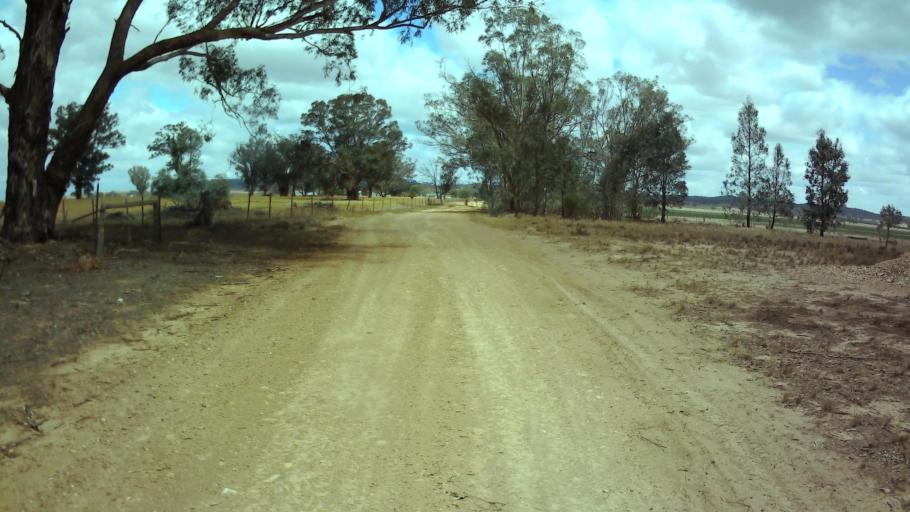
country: AU
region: New South Wales
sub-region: Weddin
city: Grenfell
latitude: -33.9795
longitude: 148.2655
